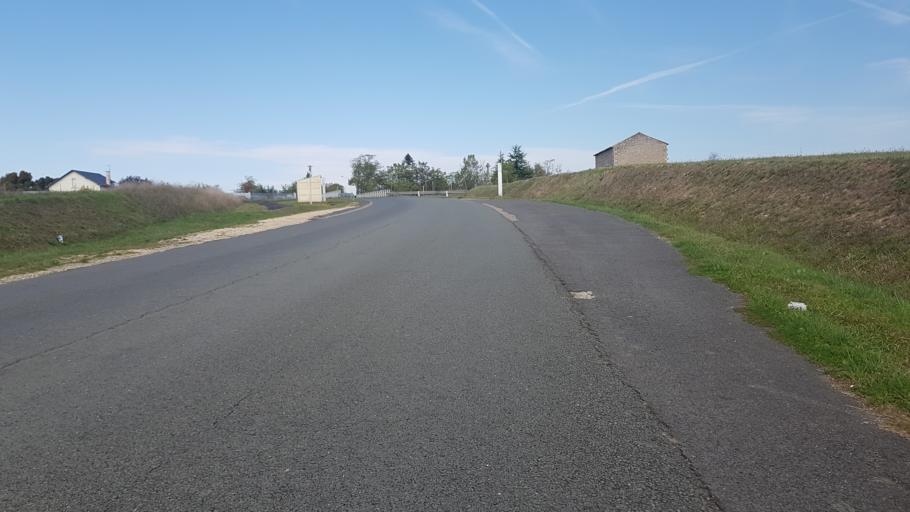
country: FR
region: Poitou-Charentes
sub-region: Departement de la Vienne
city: Chasseneuil-du-Poitou
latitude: 46.6400
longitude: 0.3557
